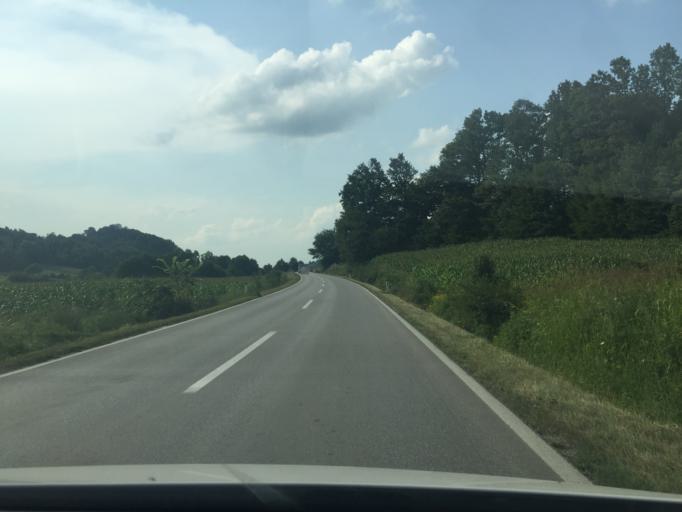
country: BA
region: Federation of Bosnia and Herzegovina
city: Mionica
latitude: 44.8120
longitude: 18.4738
